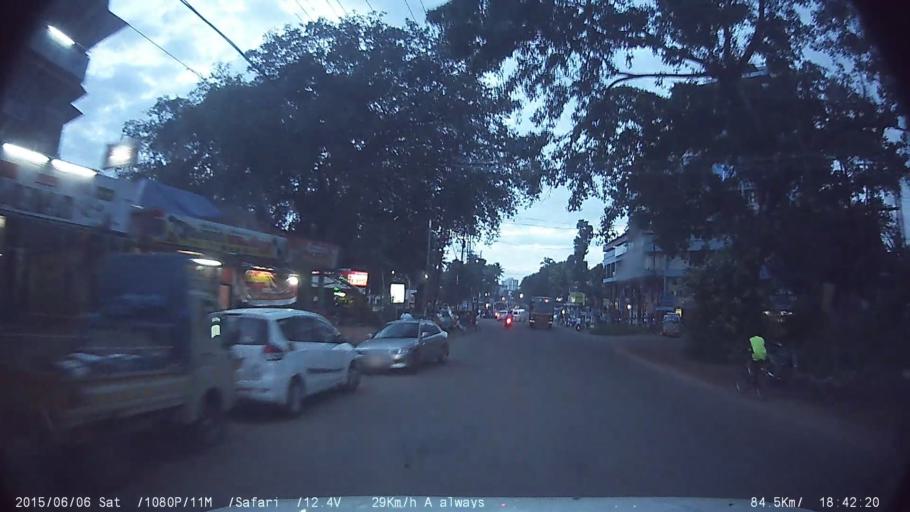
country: IN
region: Kerala
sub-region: Pattanamtitta
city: Tiruvalla
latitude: 9.3971
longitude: 76.5672
